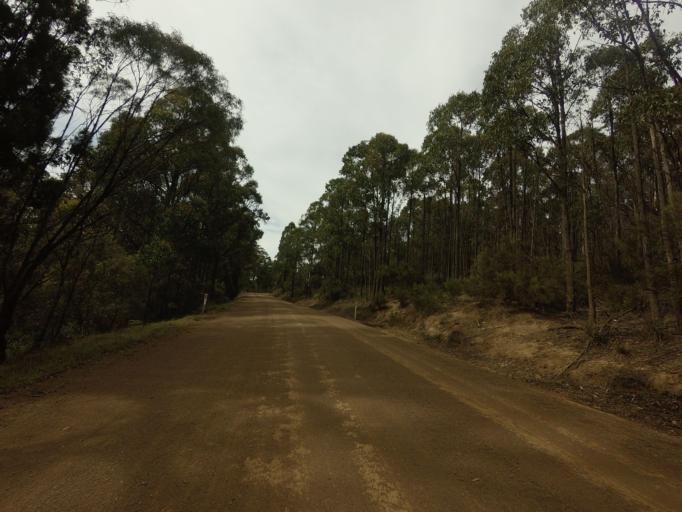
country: AU
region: Tasmania
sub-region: Sorell
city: Sorell
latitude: -42.4869
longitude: 147.6181
